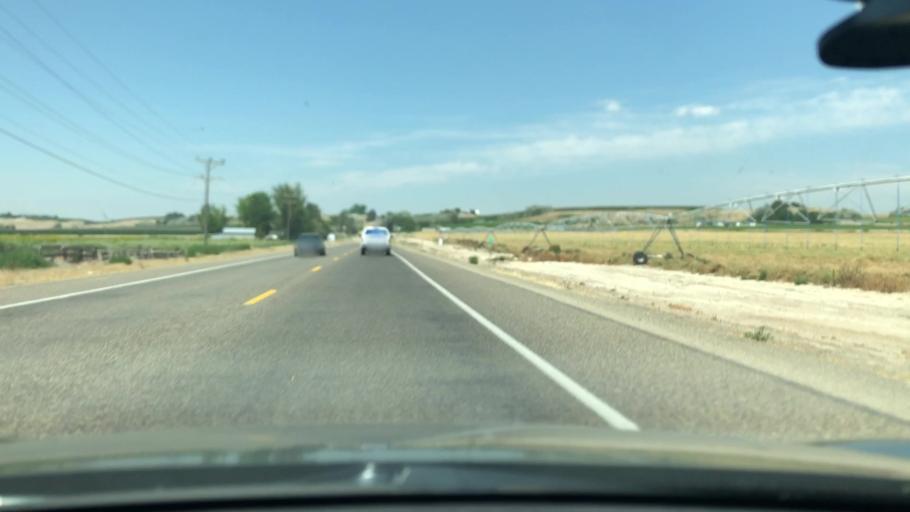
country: US
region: Idaho
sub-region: Canyon County
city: Wilder
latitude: 43.6474
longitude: -116.9117
